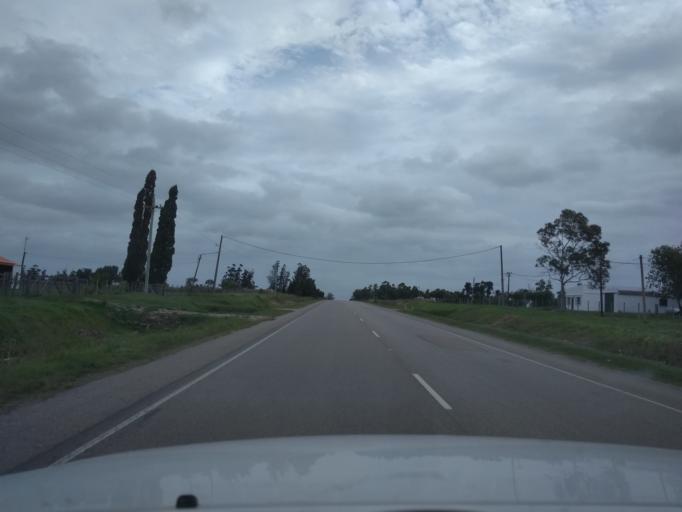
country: UY
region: Canelones
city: Tala
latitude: -34.3175
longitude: -55.7444
